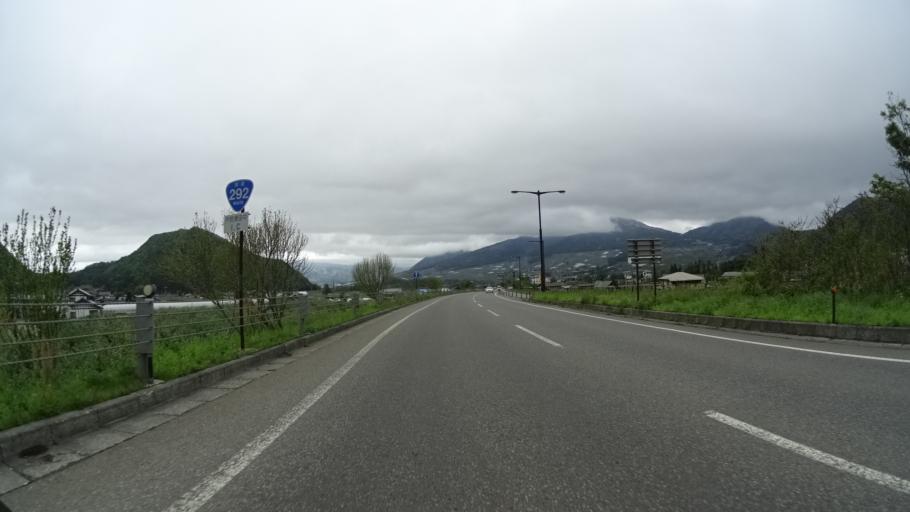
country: JP
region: Nagano
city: Nakano
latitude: 36.7434
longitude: 138.4036
